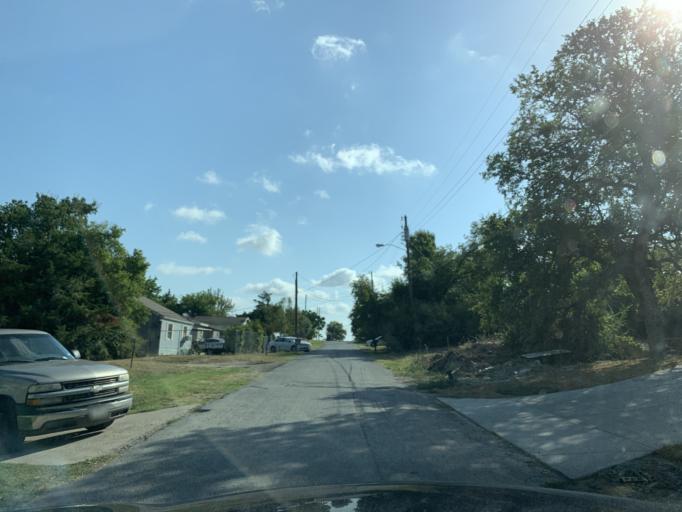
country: US
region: Texas
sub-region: Dallas County
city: Hutchins
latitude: 32.6765
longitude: -96.7769
